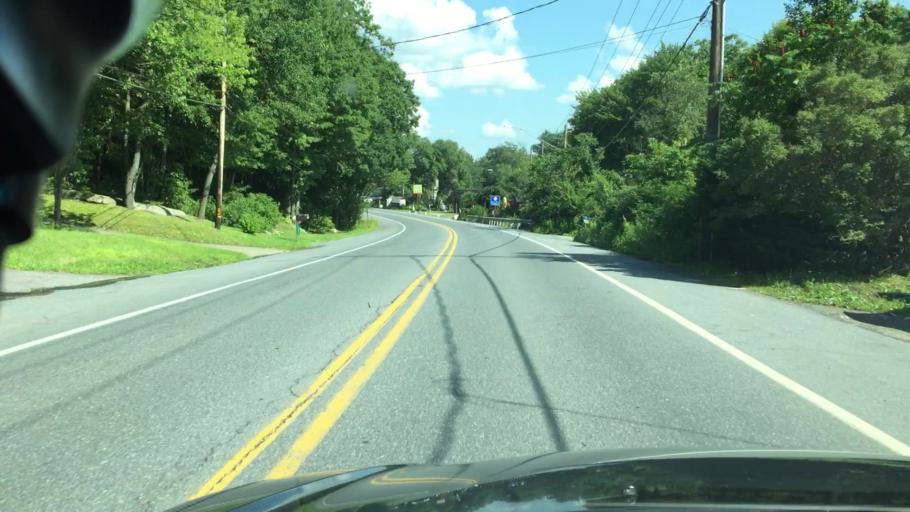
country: US
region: Pennsylvania
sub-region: Luzerne County
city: Hazleton
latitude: 40.9330
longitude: -75.9240
